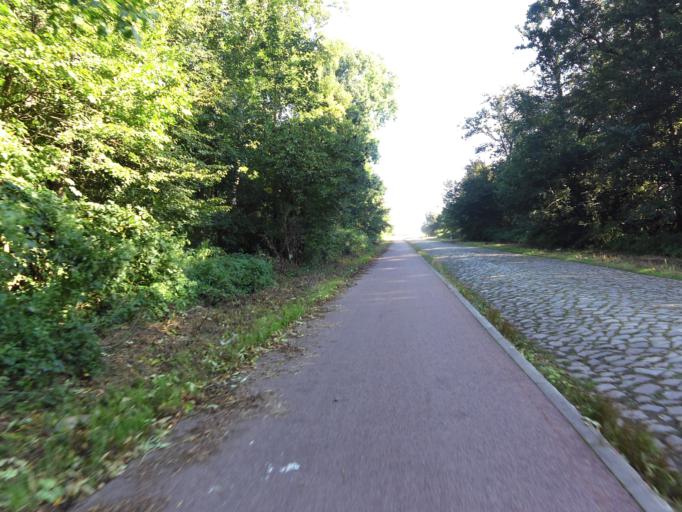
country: DE
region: Saxony-Anhalt
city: Coswig
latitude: 51.8704
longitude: 12.4460
